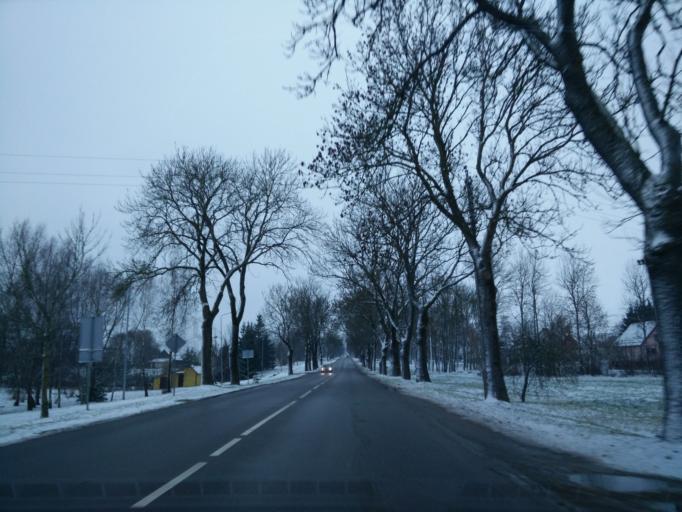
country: LT
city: Kelme
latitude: 55.6254
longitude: 22.9231
